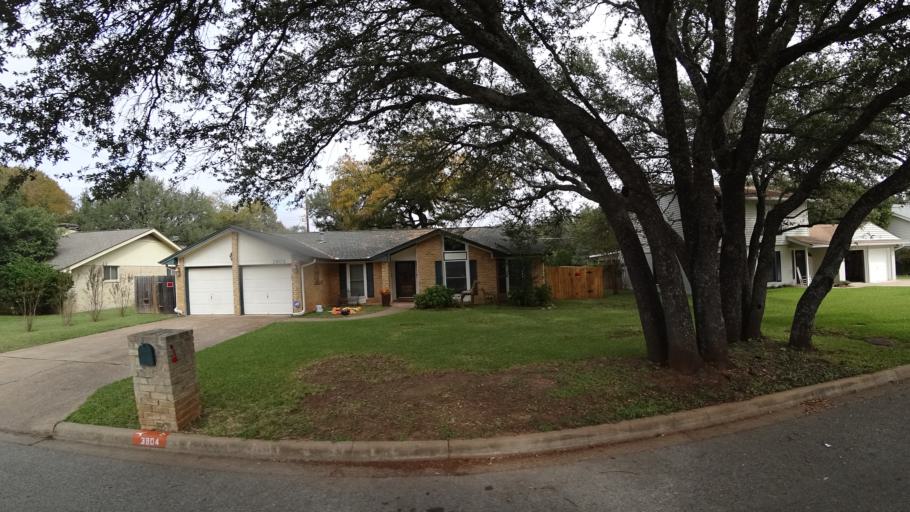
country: US
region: Texas
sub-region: Travis County
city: Wells Branch
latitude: 30.4301
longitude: -97.7092
